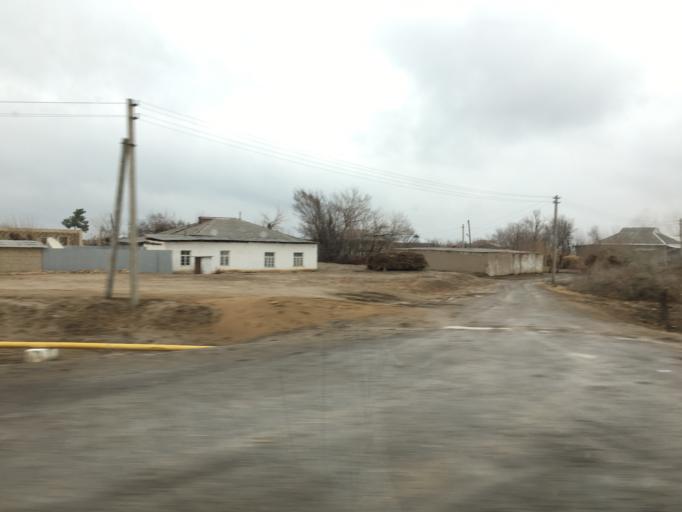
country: TM
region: Mary
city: Yoloeten
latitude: 37.3182
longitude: 62.3122
